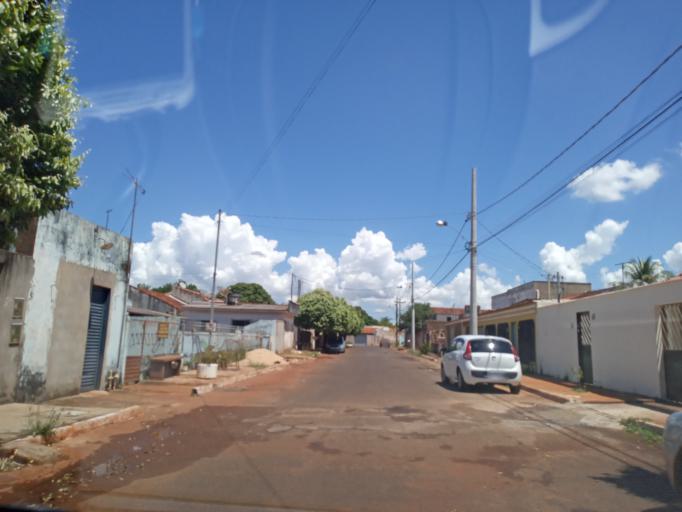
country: BR
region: Goias
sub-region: Itumbiara
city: Itumbiara
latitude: -18.4332
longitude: -49.1874
